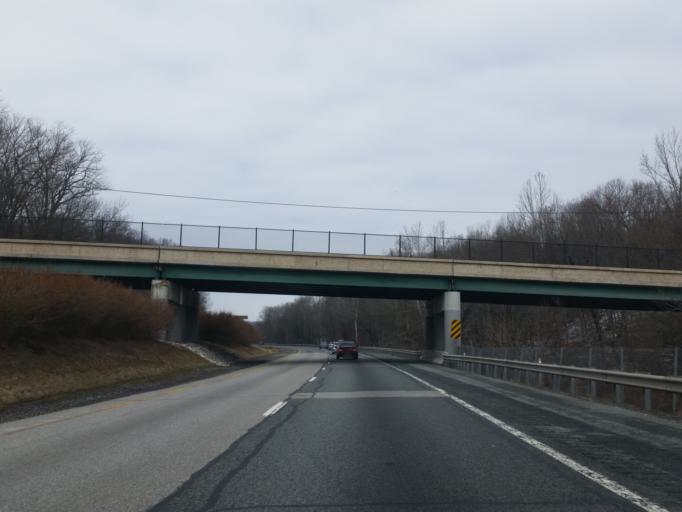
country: US
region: Maryland
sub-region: Baltimore County
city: Hunt Valley
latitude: 39.5629
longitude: -76.6654
